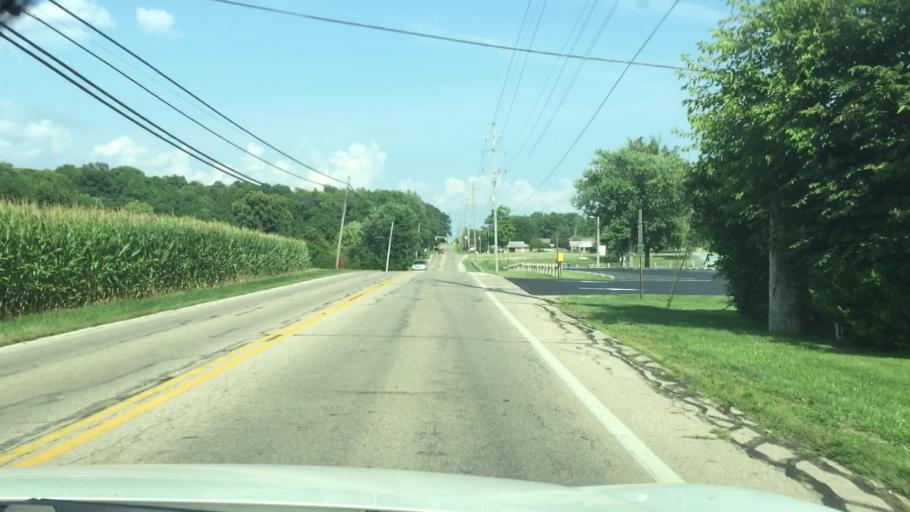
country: US
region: Ohio
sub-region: Clark County
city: Northridge
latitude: 39.9951
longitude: -83.7664
